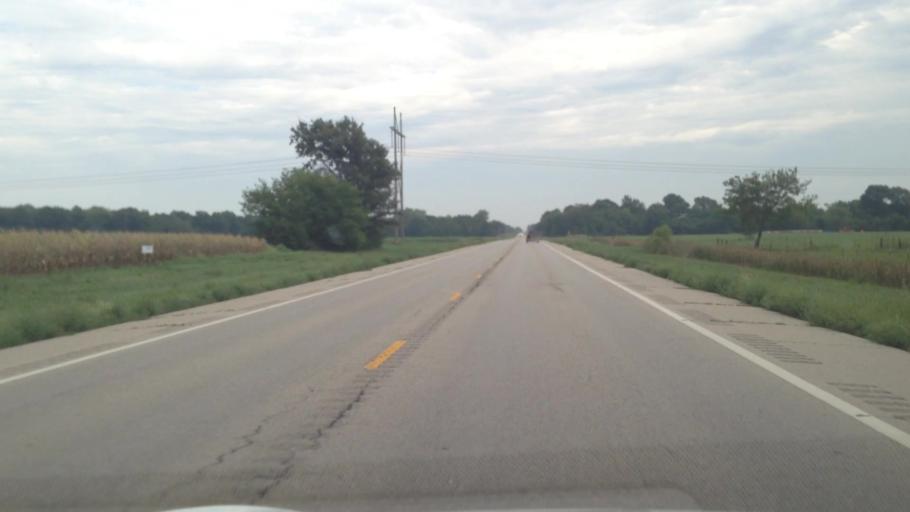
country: US
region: Kansas
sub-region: Crawford County
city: Pittsburg
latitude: 37.3392
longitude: -94.7928
